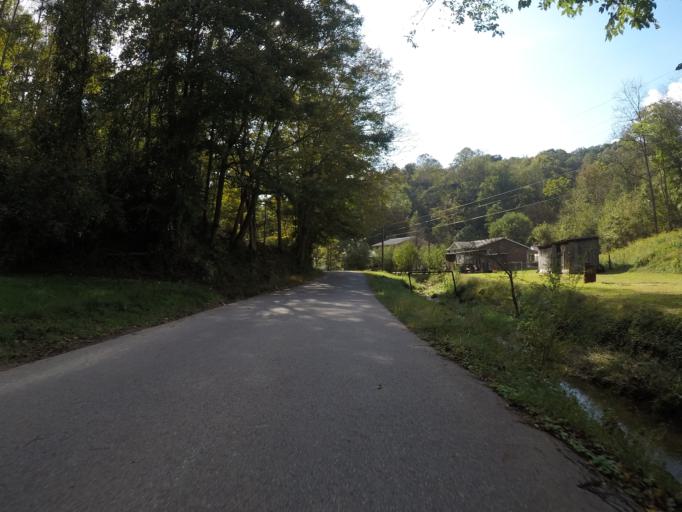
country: US
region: West Virginia
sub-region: Wayne County
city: Lavalette
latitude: 38.3589
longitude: -82.4870
